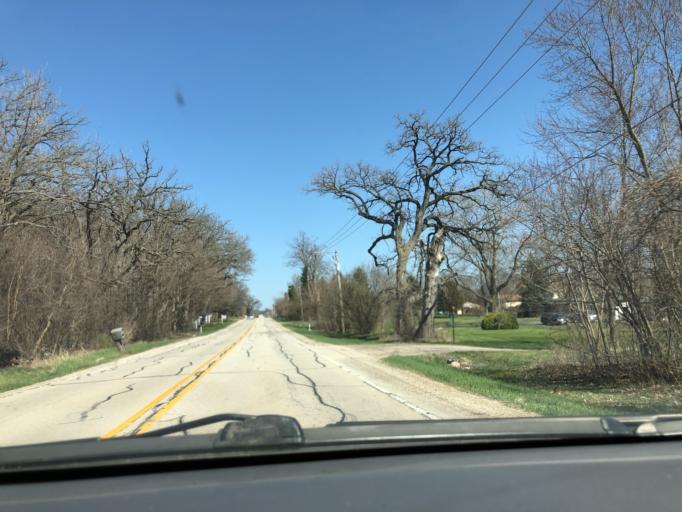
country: US
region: Illinois
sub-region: Kane County
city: Hampshire
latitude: 42.1609
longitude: -88.5180
